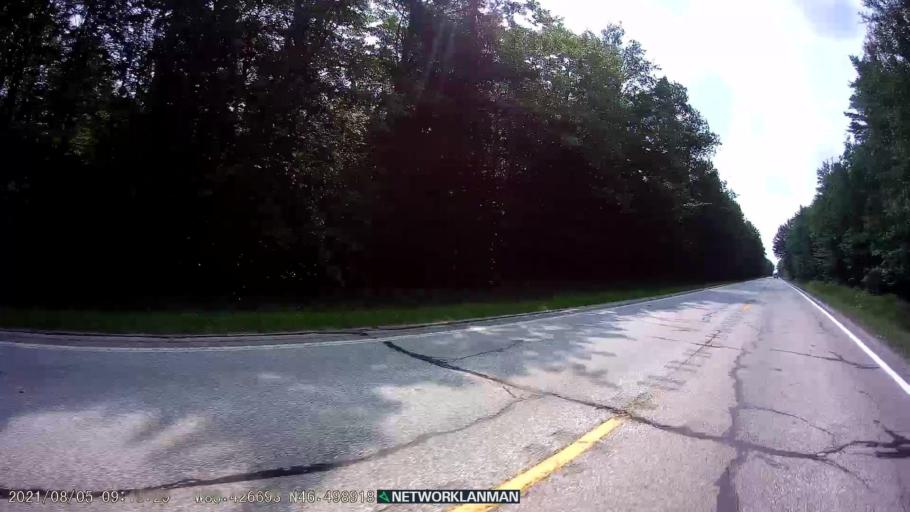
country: US
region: Michigan
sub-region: Luce County
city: Newberry
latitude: 46.4986
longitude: -85.4268
